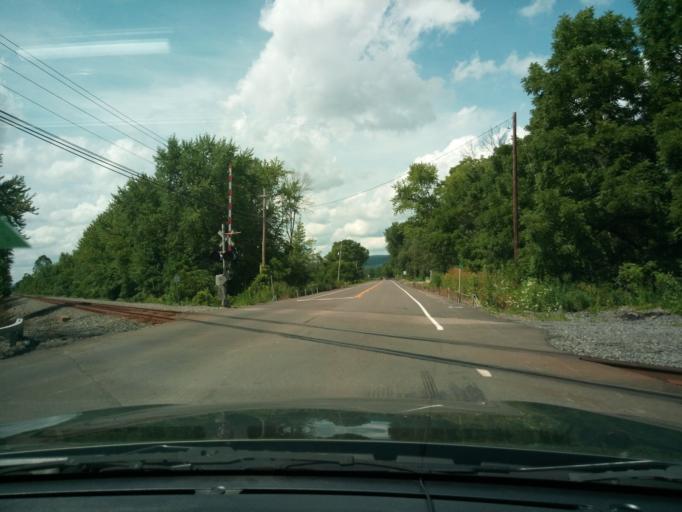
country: US
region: New York
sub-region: Chemung County
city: Southport
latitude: 42.0243
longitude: -76.7413
